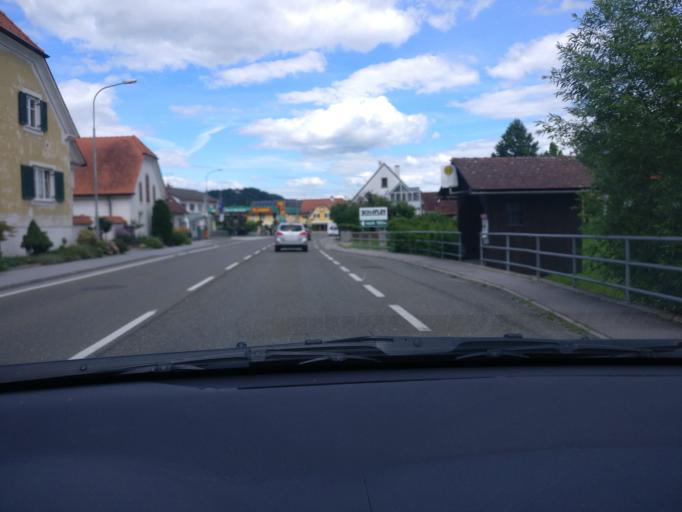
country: AT
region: Styria
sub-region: Politischer Bezirk Hartberg-Fuerstenfeld
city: Kaibing
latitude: 47.1932
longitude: 15.8262
